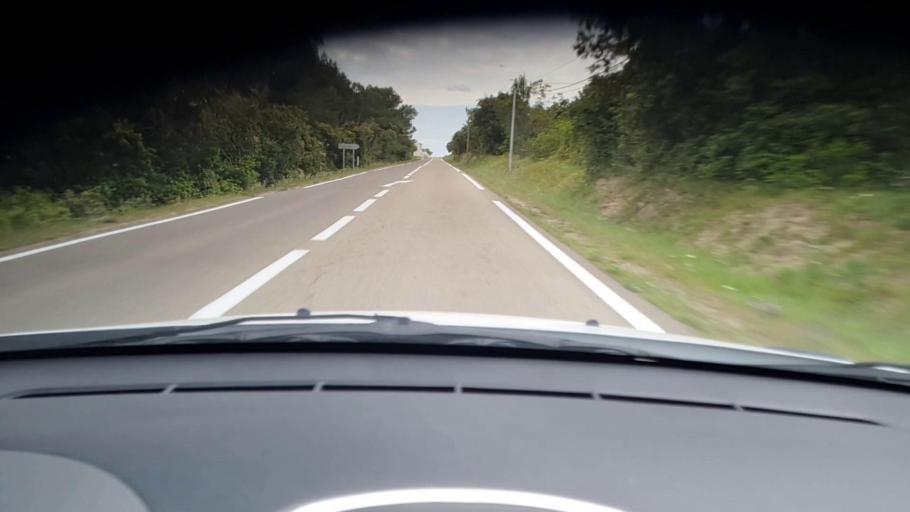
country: FR
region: Languedoc-Roussillon
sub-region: Departement du Gard
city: Poulx
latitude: 43.8798
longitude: 4.3795
